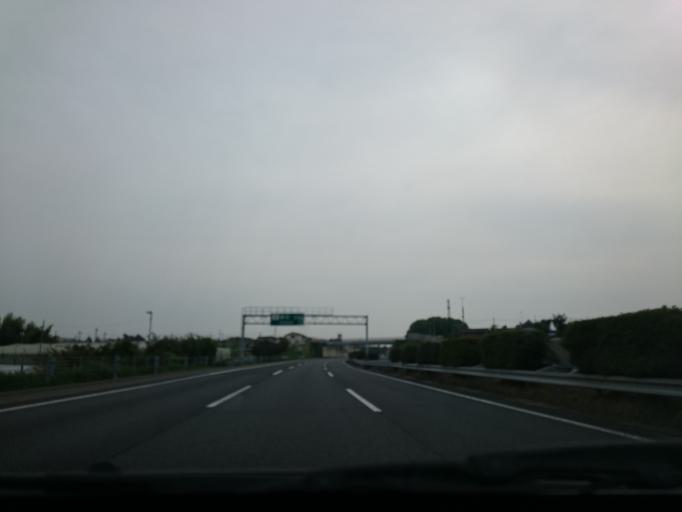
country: JP
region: Tochigi
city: Utsunomiya-shi
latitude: 36.5570
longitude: 139.8141
